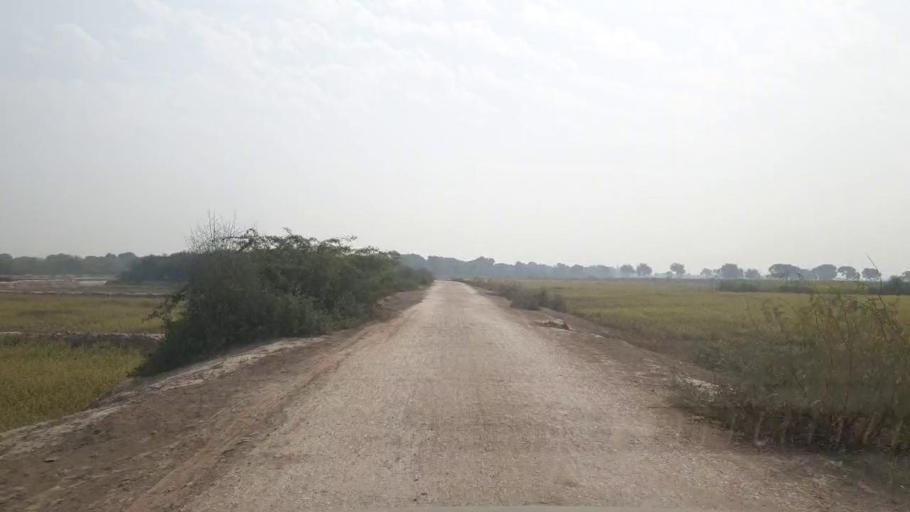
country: PK
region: Sindh
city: Hala
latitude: 25.7826
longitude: 68.4349
